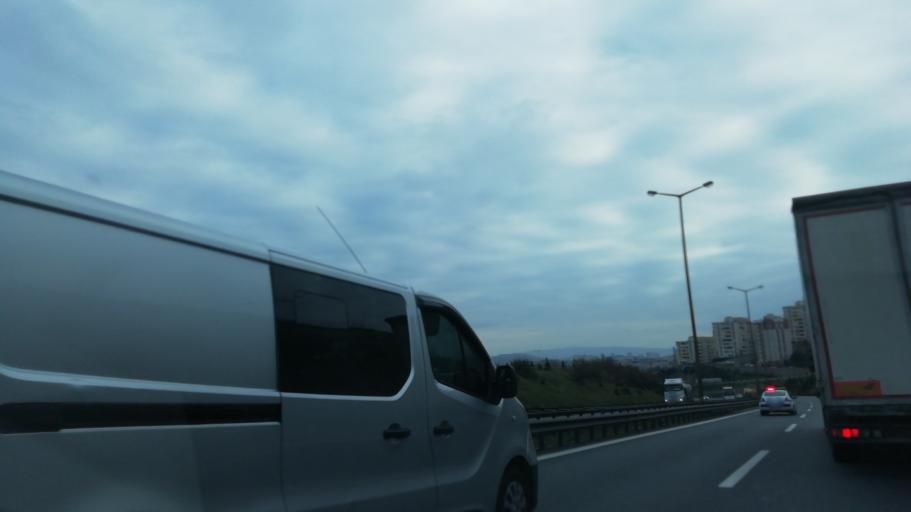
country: TR
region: Kocaeli
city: Izmit
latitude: 40.7831
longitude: 29.9352
